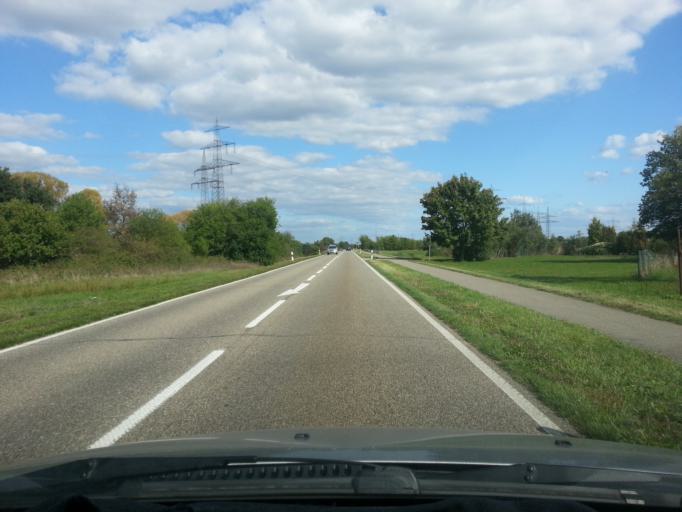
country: DE
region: Baden-Wuerttemberg
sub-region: Karlsruhe Region
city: Philippsburg
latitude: 49.2431
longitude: 8.4762
